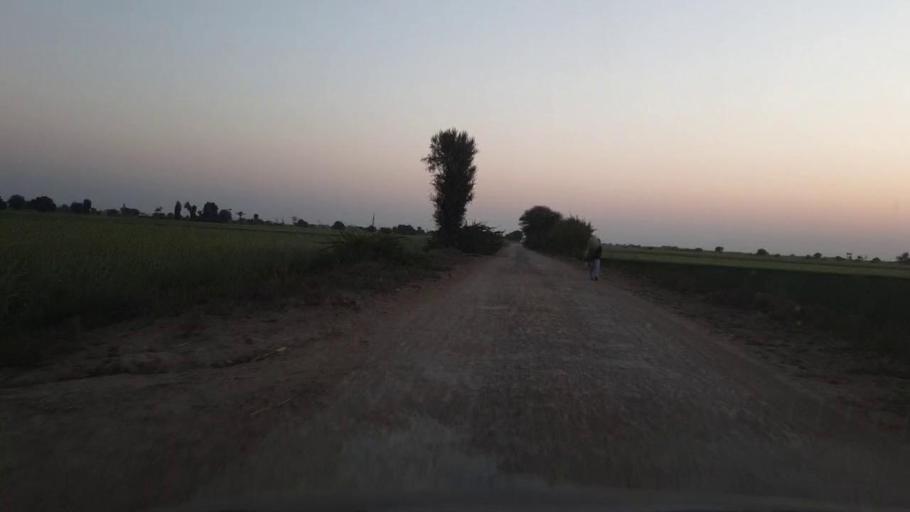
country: PK
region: Sindh
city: Digri
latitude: 25.1901
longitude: 69.1889
